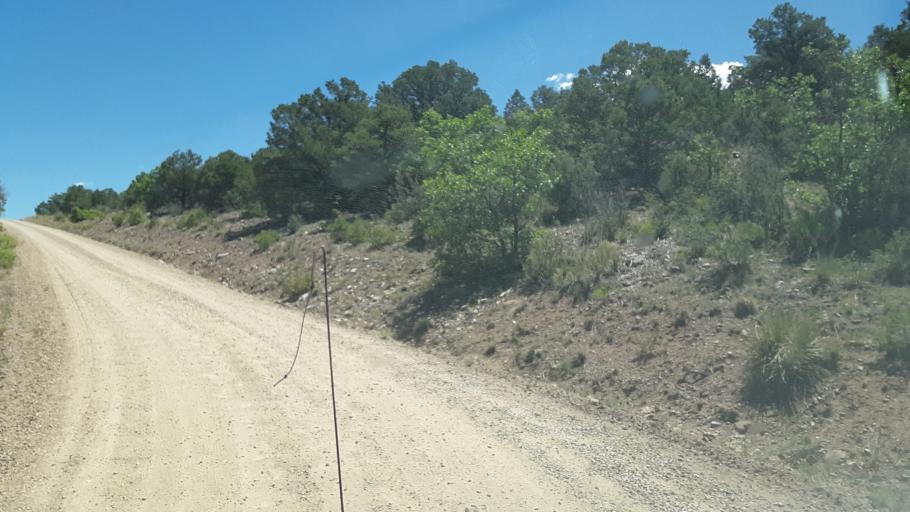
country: US
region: Colorado
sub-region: Custer County
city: Westcliffe
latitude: 38.3019
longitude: -105.6698
